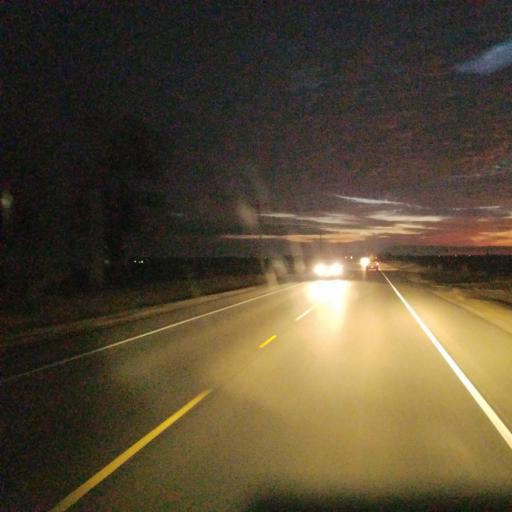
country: US
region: Illinois
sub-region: Peoria County
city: Hanna City
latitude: 40.6975
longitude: -89.8664
